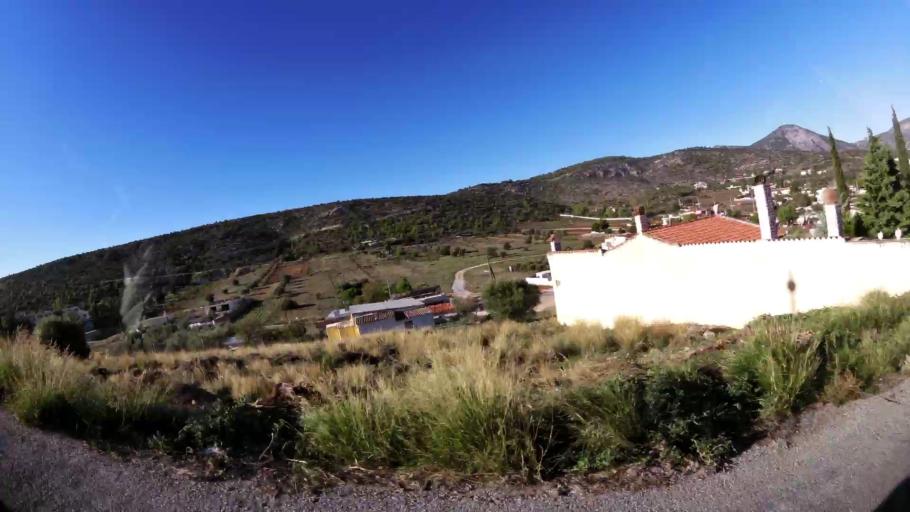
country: GR
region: Attica
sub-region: Nomarchia Anatolikis Attikis
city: Koropi
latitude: 37.8943
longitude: 23.8673
